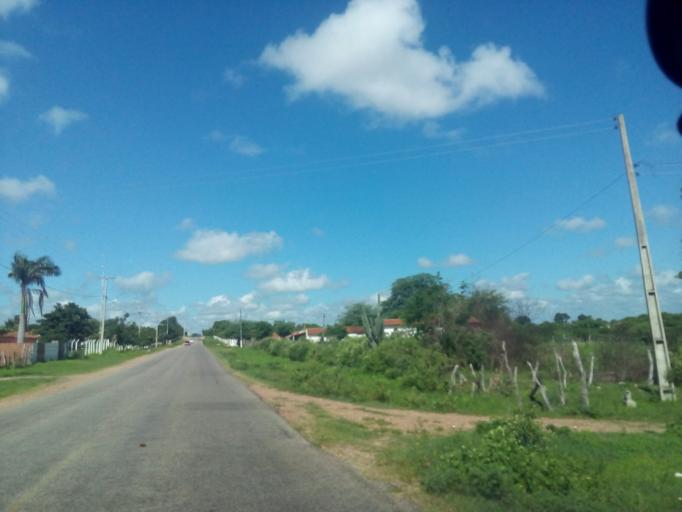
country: BR
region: Rio Grande do Norte
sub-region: Sao Paulo Do Potengi
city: Sao Paulo do Potengi
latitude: -5.9118
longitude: -35.7008
